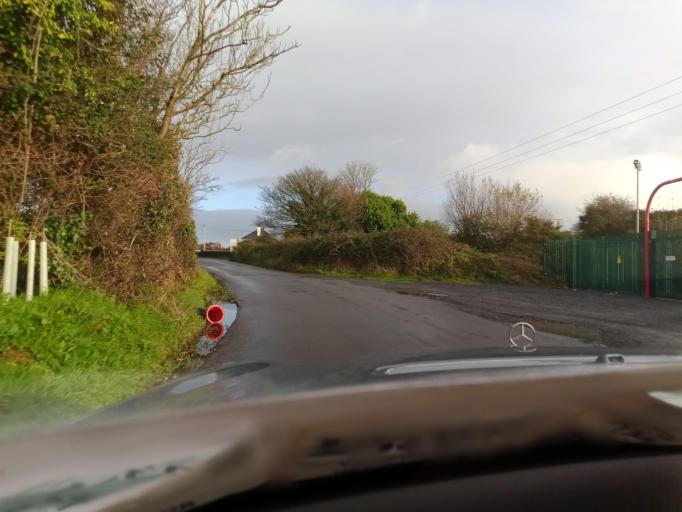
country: IE
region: Munster
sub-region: Waterford
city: Waterford
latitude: 52.2794
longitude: -7.1707
